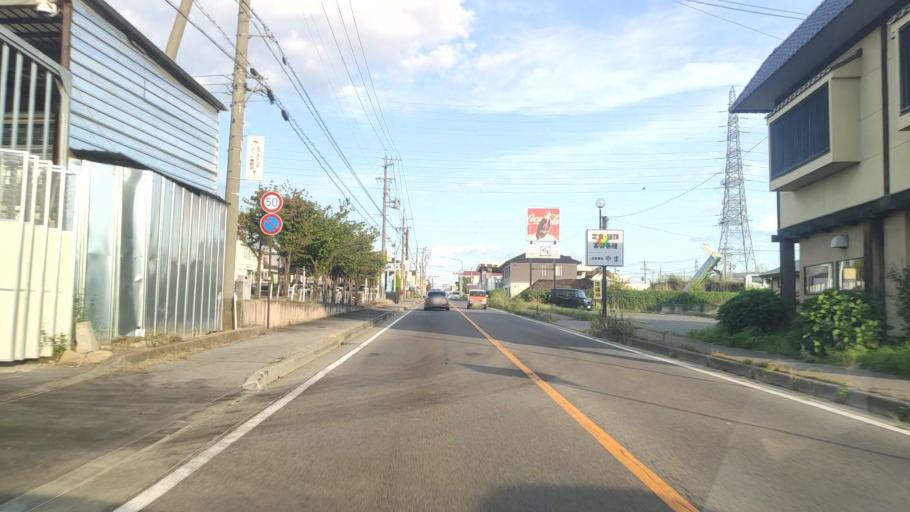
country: JP
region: Nagano
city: Kamimaruko
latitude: 36.3521
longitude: 138.3525
